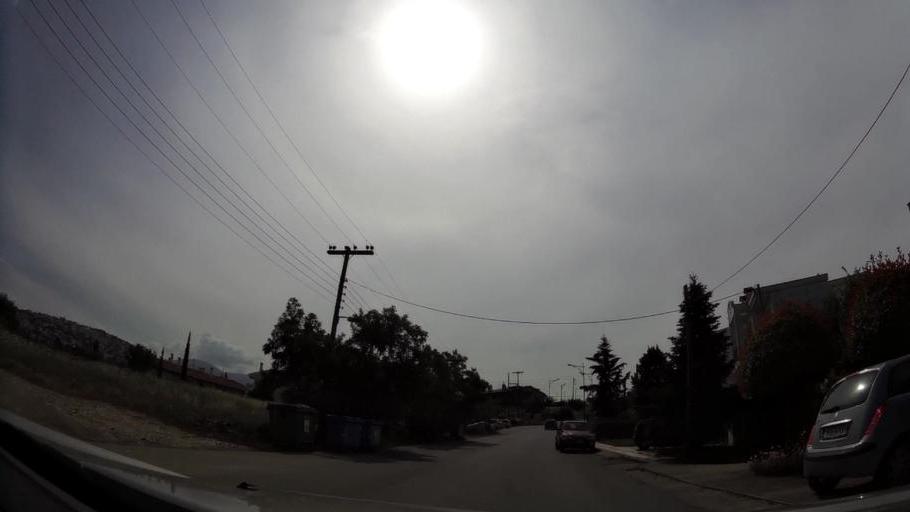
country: GR
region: Central Macedonia
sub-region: Nomos Thessalonikis
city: Panorama
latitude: 40.5804
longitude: 23.0100
